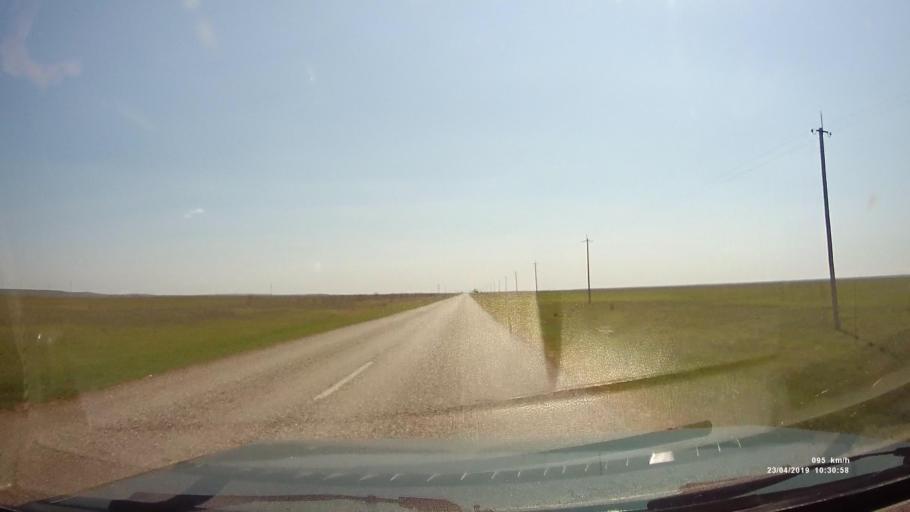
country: RU
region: Kalmykiya
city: Yashalta
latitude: 46.5887
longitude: 42.5542
